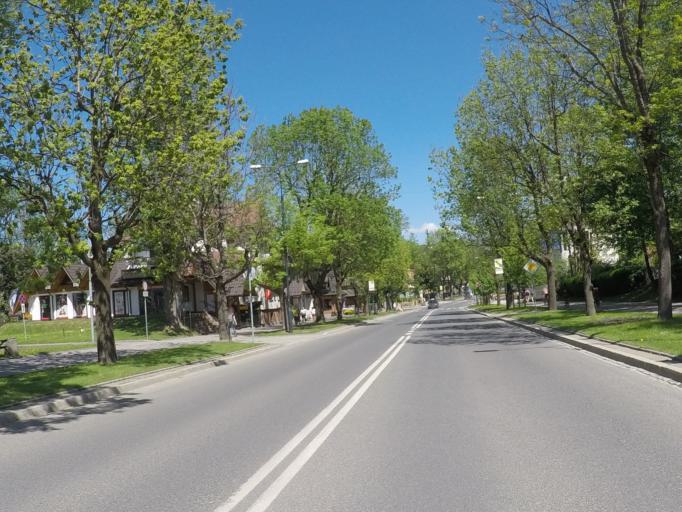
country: PL
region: Lesser Poland Voivodeship
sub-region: Powiat tatrzanski
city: Zakopane
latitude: 49.2976
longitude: 19.9568
